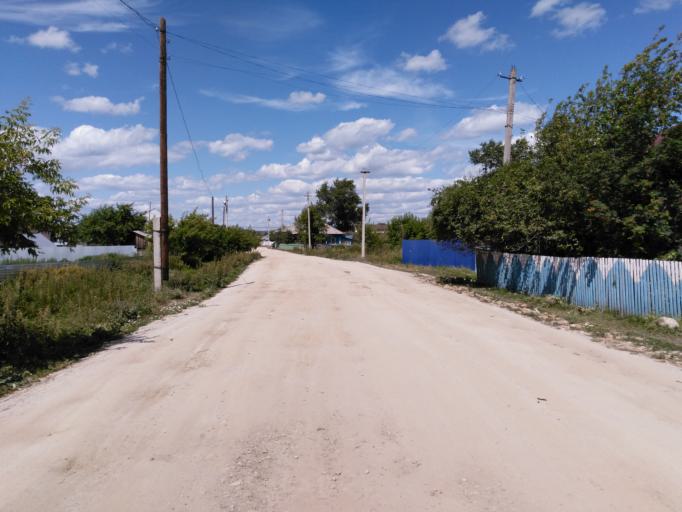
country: RU
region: Bashkortostan
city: Akhunovo
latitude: 54.2084
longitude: 59.6072
